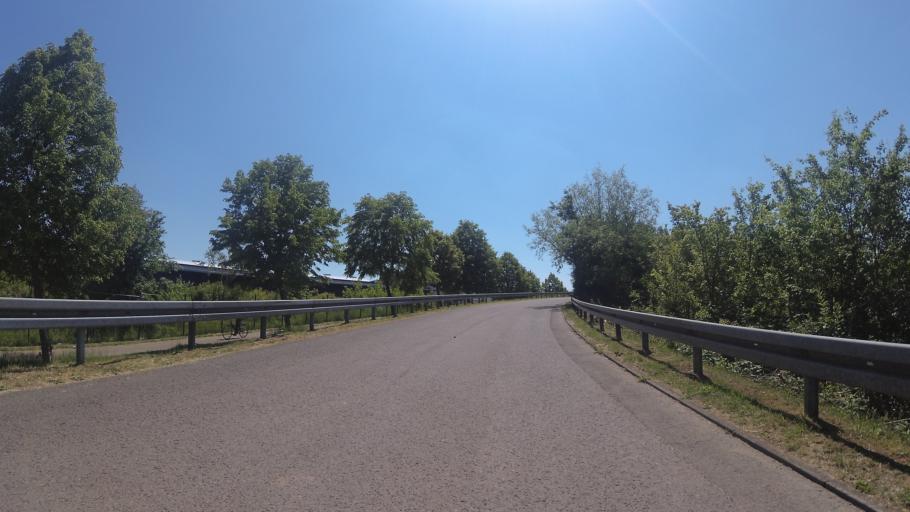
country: DE
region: Saarland
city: Mettlach
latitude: 49.4695
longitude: 6.6081
